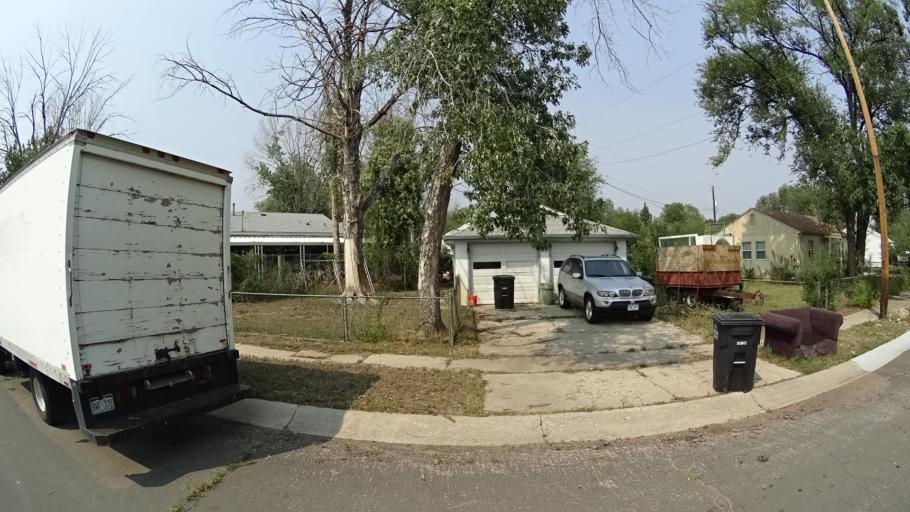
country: US
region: Colorado
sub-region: El Paso County
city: Colorado Springs
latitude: 38.8089
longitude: -104.8135
